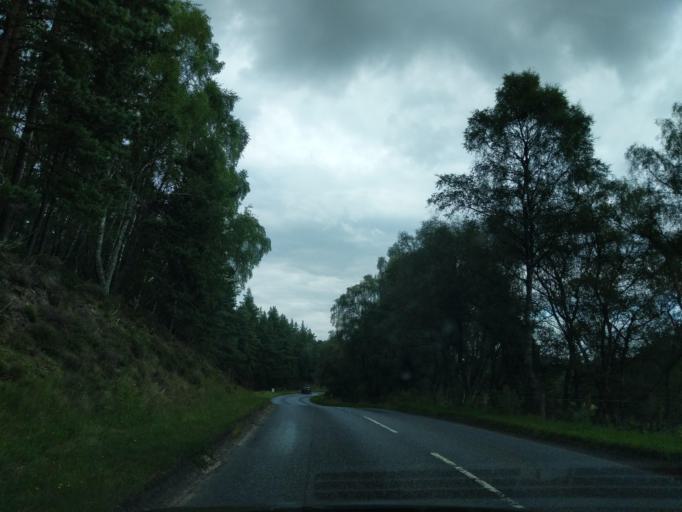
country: GB
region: Scotland
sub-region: Highland
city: Aviemore
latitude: 57.2942
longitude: -3.7895
